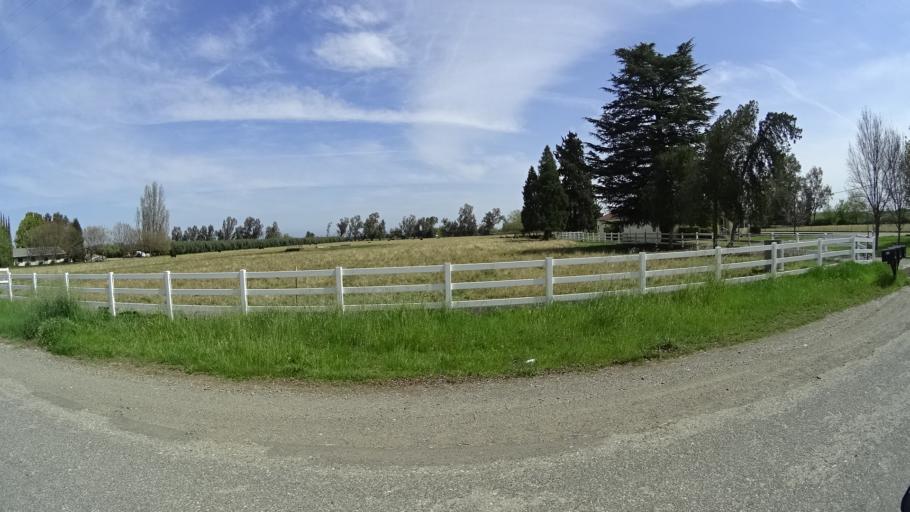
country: US
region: California
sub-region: Glenn County
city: Orland
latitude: 39.7915
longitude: -122.1504
